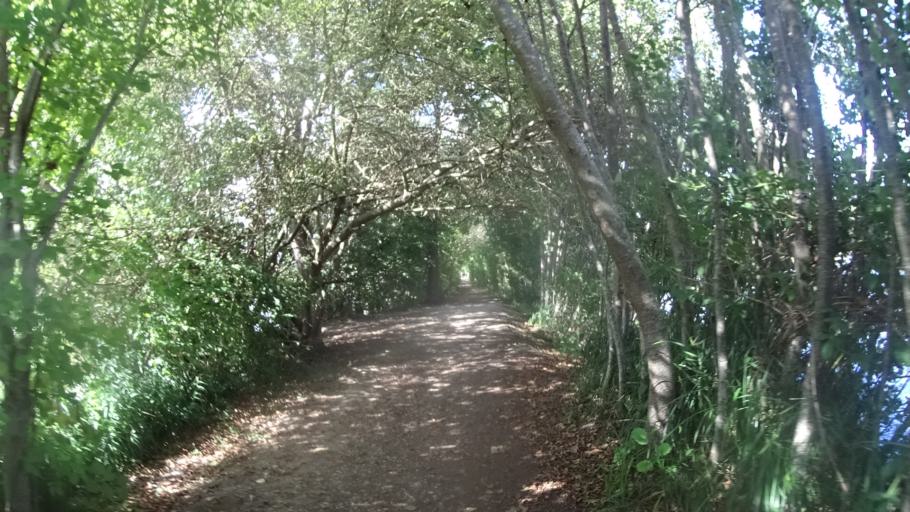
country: FR
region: Ile-de-France
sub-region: Departement de l'Essonne
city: Vert-le-Petit
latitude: 48.5426
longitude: 2.3711
